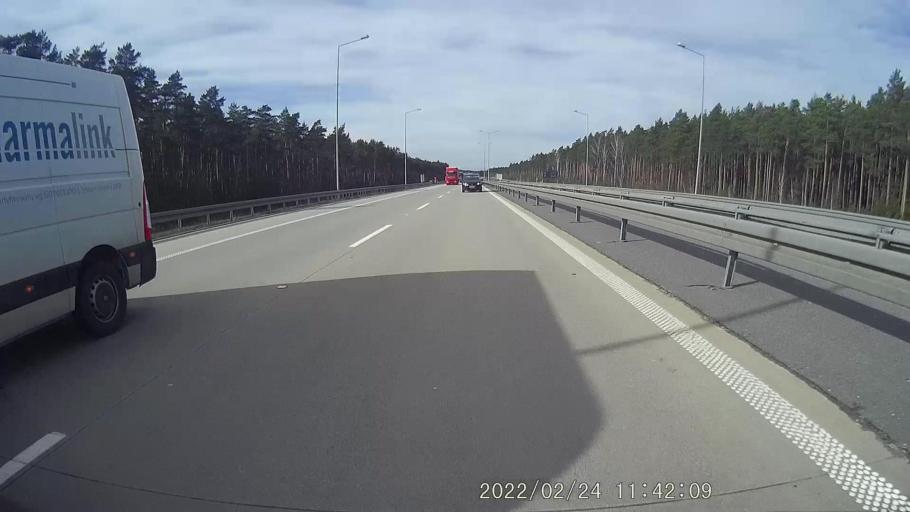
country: PL
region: Lower Silesian Voivodeship
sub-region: Powiat polkowicki
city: Radwanice
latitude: 51.5465
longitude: 15.9016
